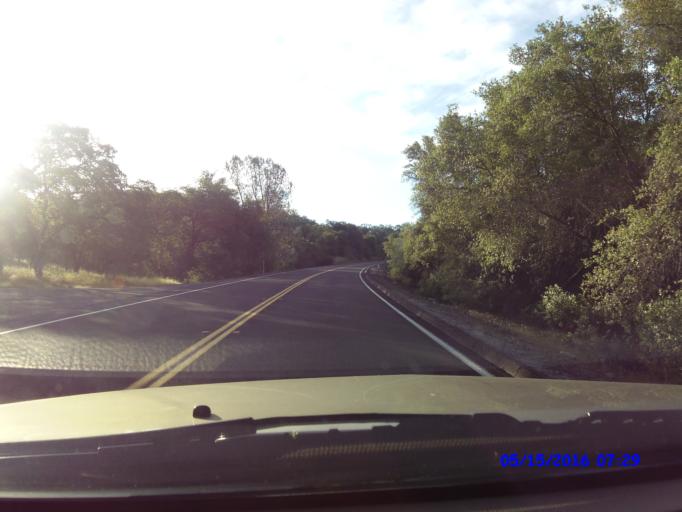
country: US
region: California
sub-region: Tuolumne County
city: Tuolumne City
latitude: 37.7327
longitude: -120.2147
